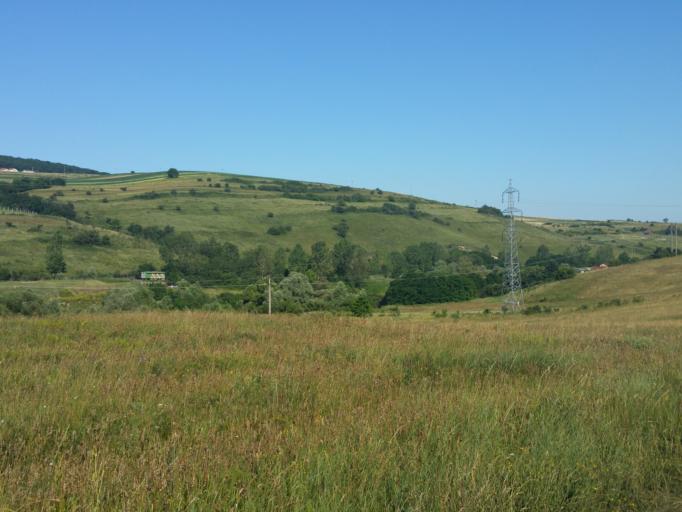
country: RO
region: Cluj
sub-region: Comuna Baciu
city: Baciu
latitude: 46.8073
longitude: 23.5263
